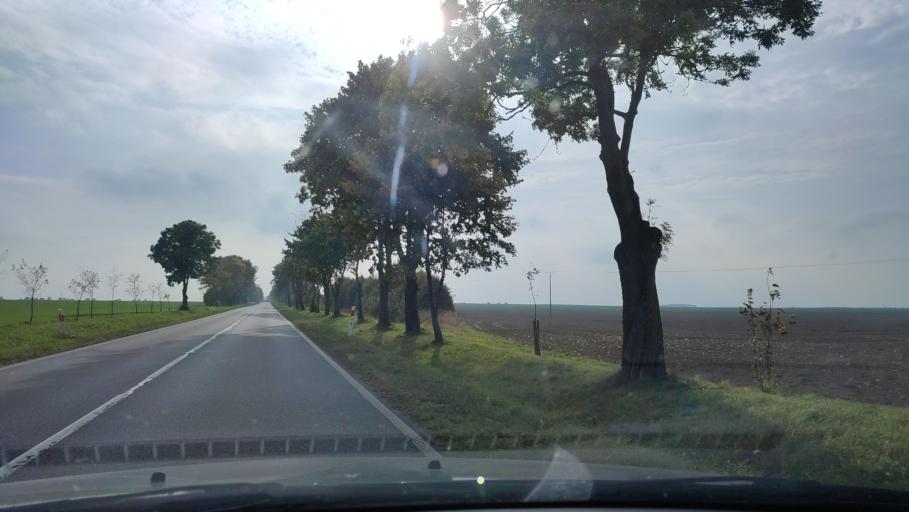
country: PL
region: Warmian-Masurian Voivodeship
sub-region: Powiat nidzicki
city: Kozlowo
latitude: 53.3234
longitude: 20.3129
